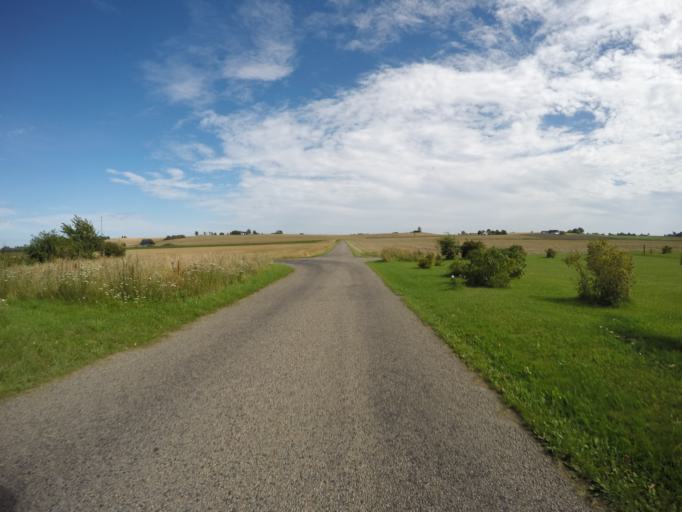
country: SE
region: Skane
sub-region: Simrishamns Kommun
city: Simrishamn
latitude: 55.4967
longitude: 14.2380
